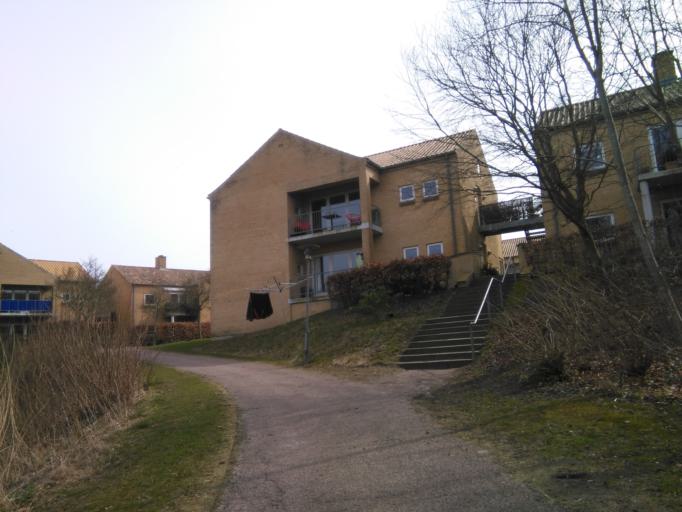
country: DK
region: Central Jutland
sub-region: Arhus Kommune
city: Beder
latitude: 56.1046
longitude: 10.2203
